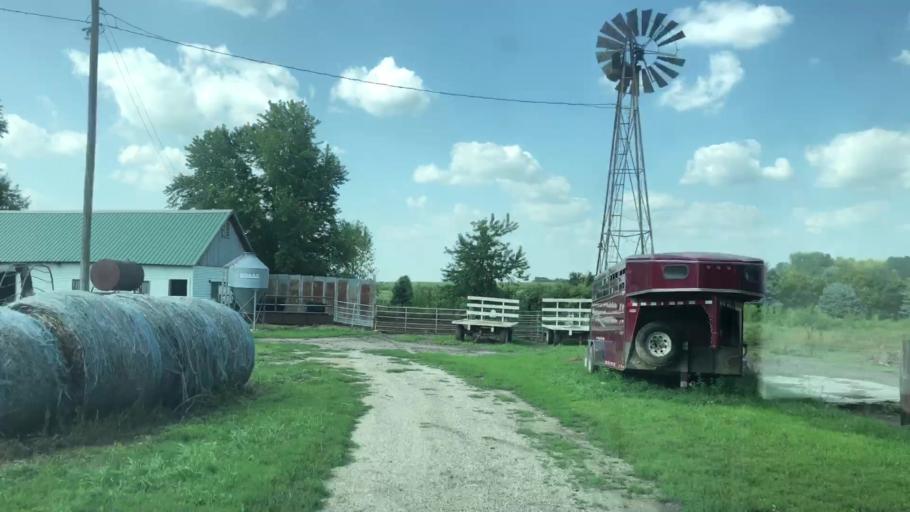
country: US
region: Iowa
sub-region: O'Brien County
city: Sheldon
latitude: 43.1578
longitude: -95.7837
